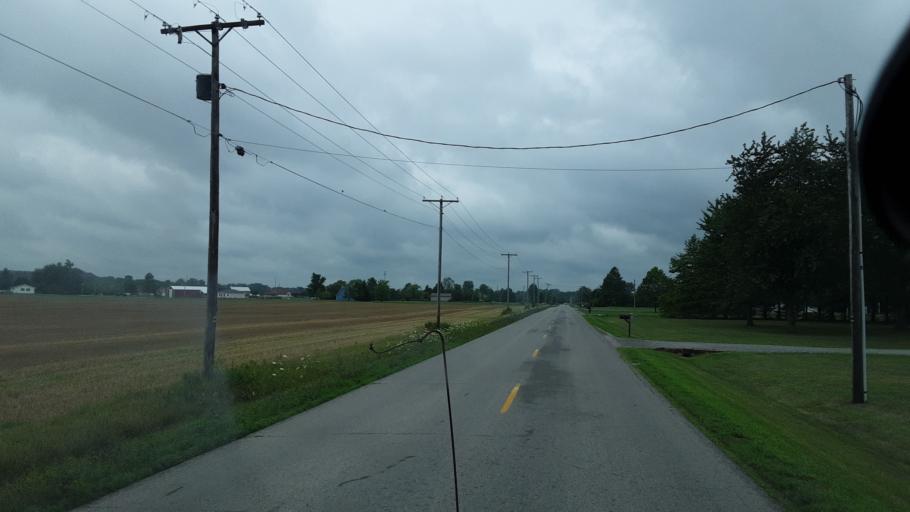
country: US
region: Indiana
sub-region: Allen County
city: New Haven
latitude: 40.9470
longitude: -85.0423
